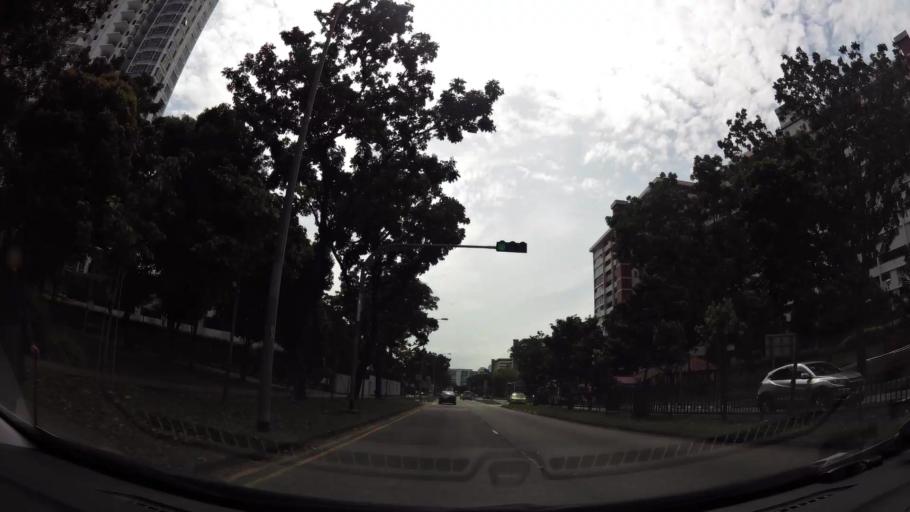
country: SG
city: Singapore
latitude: 1.3094
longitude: 103.7602
